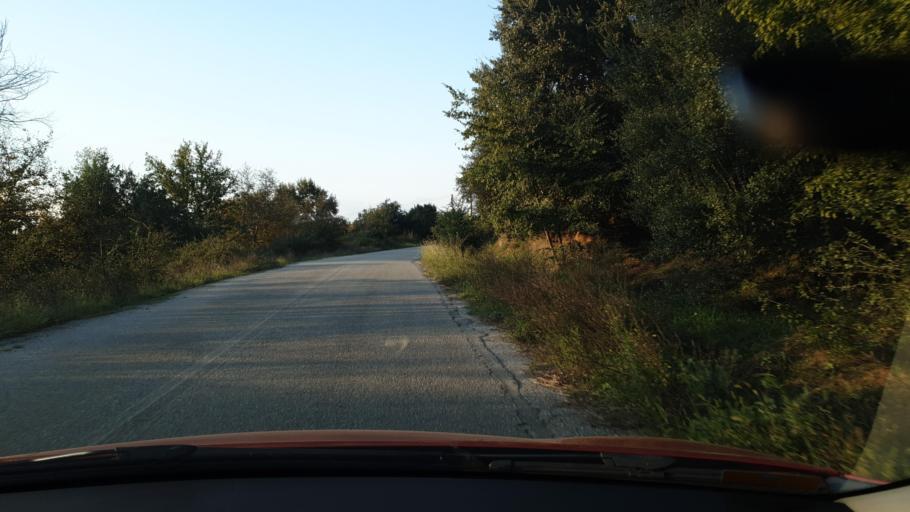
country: GR
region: Central Macedonia
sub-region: Nomos Thessalonikis
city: Nea Apollonia
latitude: 40.5519
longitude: 23.4515
